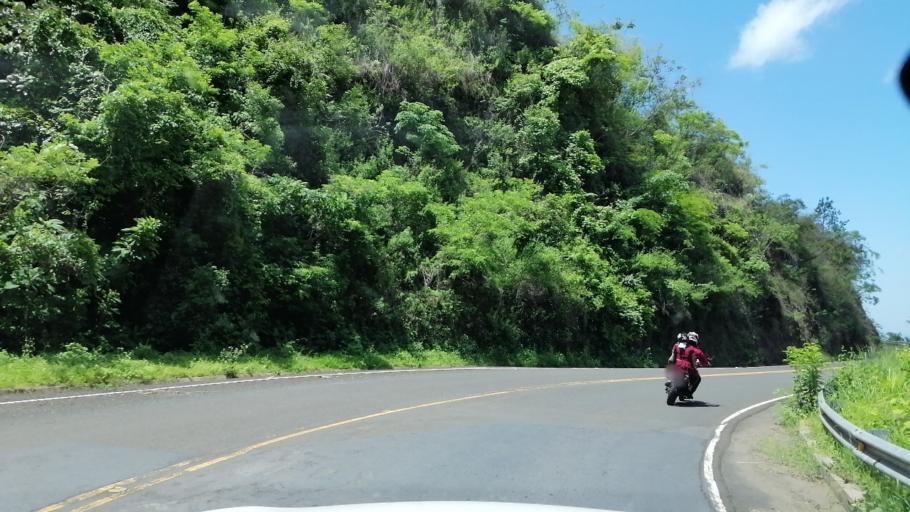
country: SV
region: San Miguel
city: Ciudad Barrios
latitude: 13.7935
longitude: -88.2899
